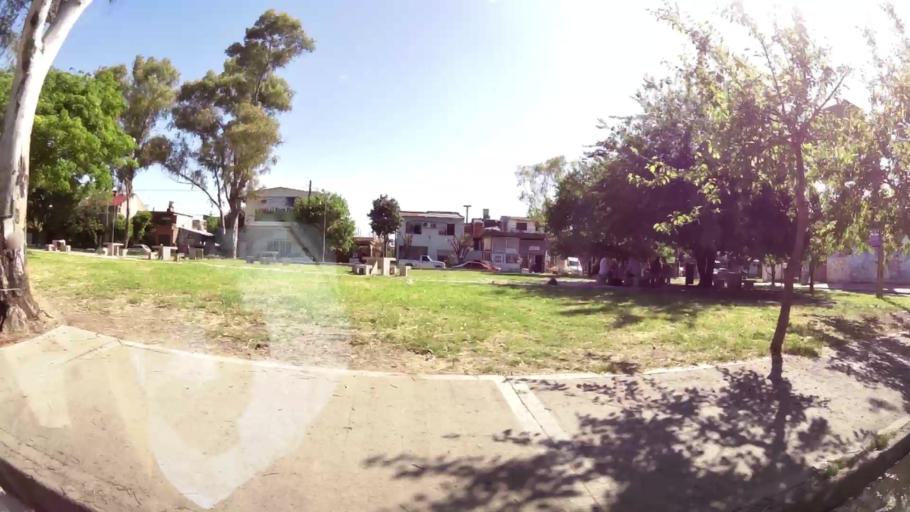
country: AR
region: Buenos Aires
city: Caseros
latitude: -34.5412
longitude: -58.5908
